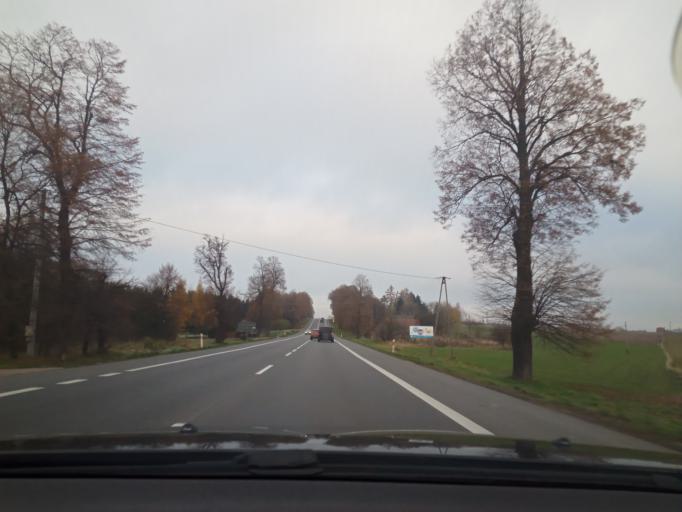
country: PL
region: Lesser Poland Voivodeship
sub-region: Powiat miechowski
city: Miechow
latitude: 50.3397
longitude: 20.0346
